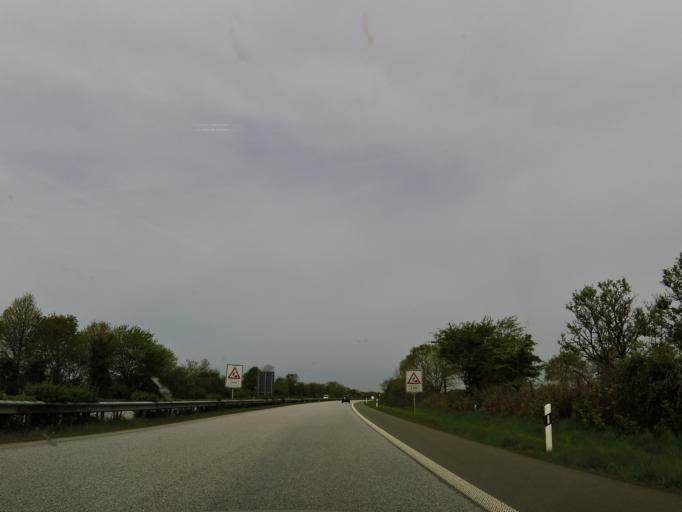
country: DE
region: Schleswig-Holstein
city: Schafstedt
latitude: 54.0775
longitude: 9.2764
